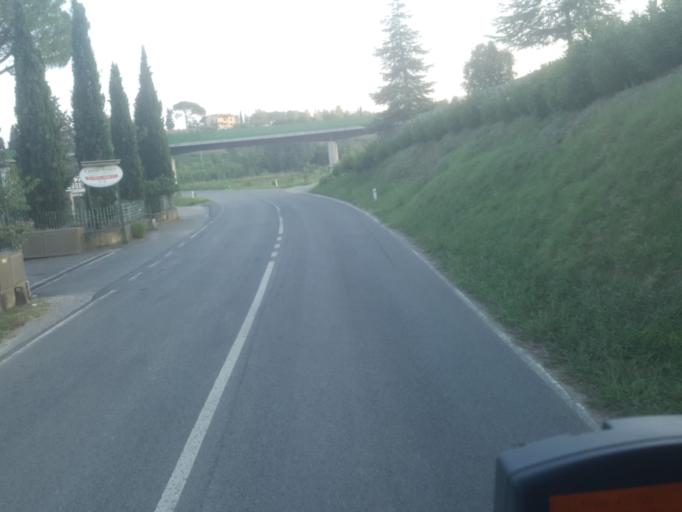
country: IT
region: Tuscany
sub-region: Province of Florence
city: Certaldo
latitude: 43.5345
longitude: 11.0340
